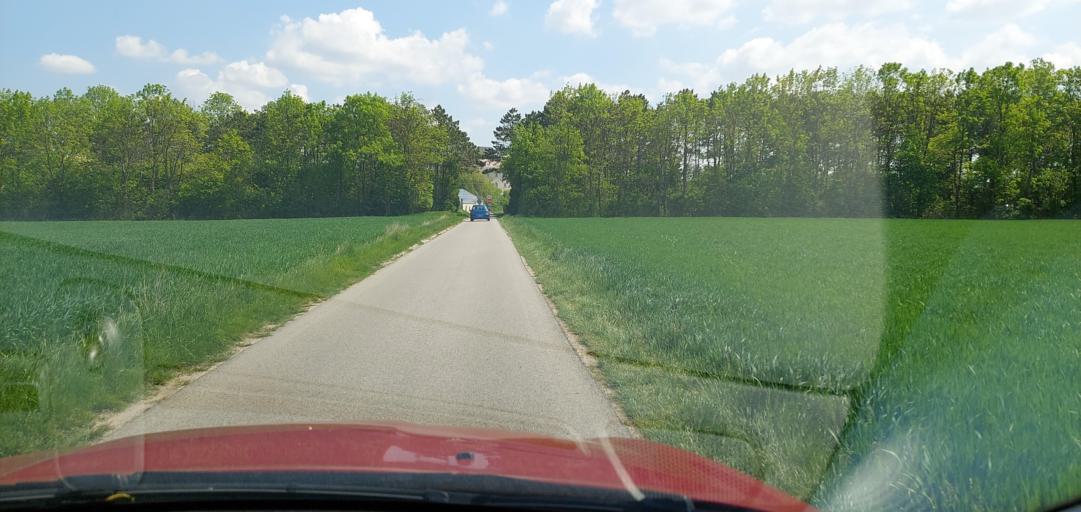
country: AT
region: Lower Austria
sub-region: Politischer Bezirk Bruck an der Leitha
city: Enzersdorf an der Fischa
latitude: 48.0850
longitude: 16.5992
